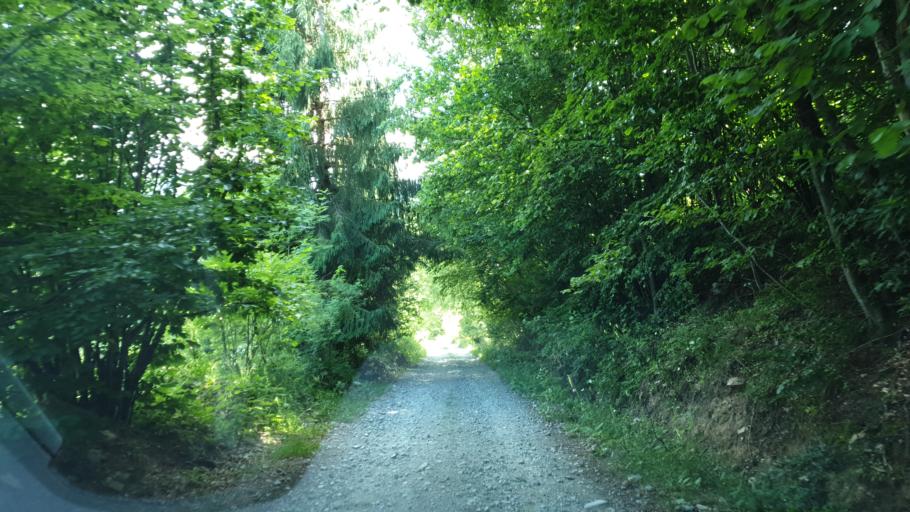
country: RO
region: Hunedoara
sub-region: Comuna Uricani
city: Uricani
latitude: 45.3085
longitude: 22.9817
